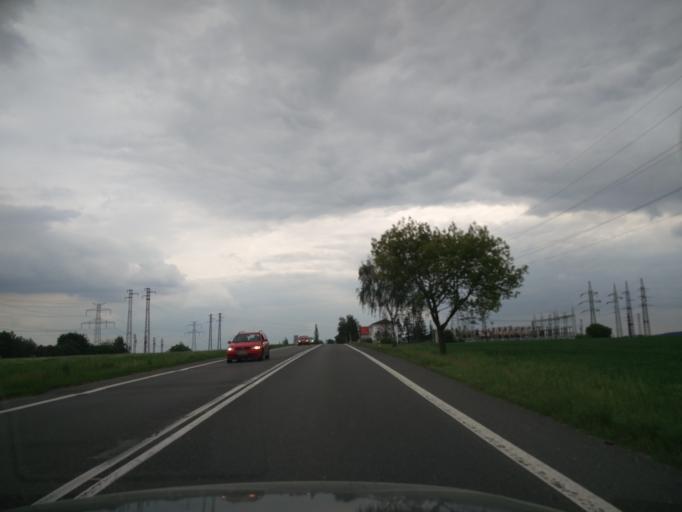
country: CZ
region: Jihocesky
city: Mirovice
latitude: 49.5174
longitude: 14.0728
